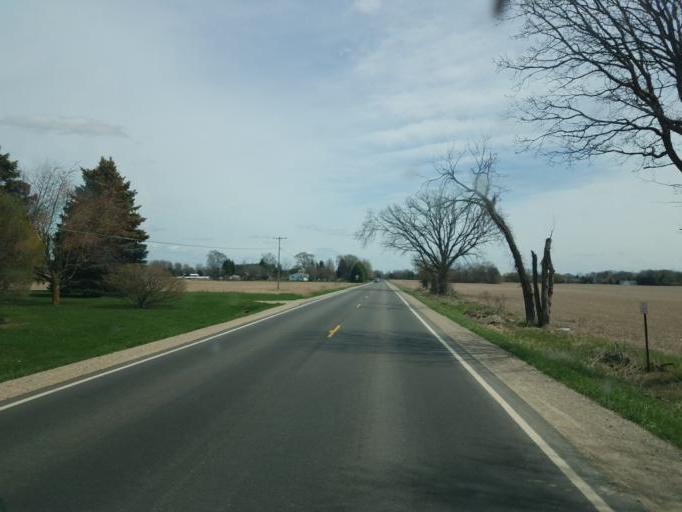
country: US
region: Michigan
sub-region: Isabella County
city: Mount Pleasant
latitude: 43.6260
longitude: -84.7973
